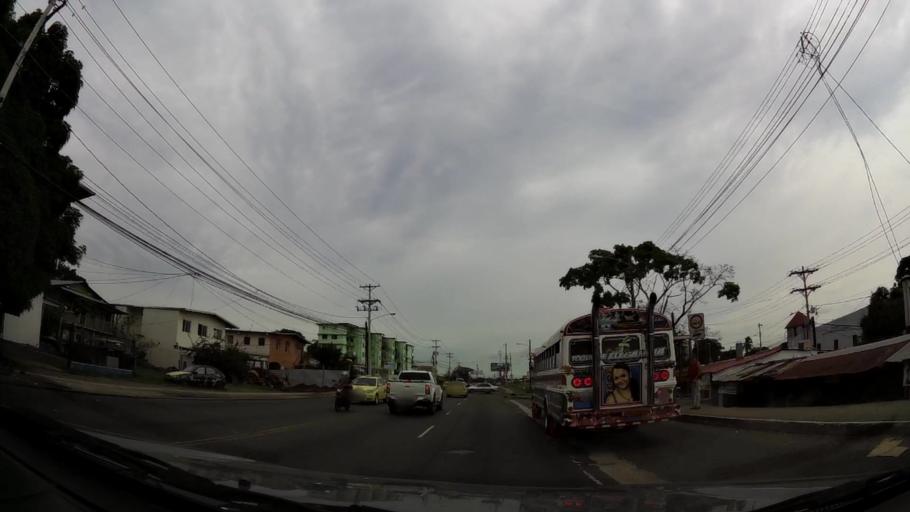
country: PA
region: Panama
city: San Miguelito
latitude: 9.0419
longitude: -79.4573
